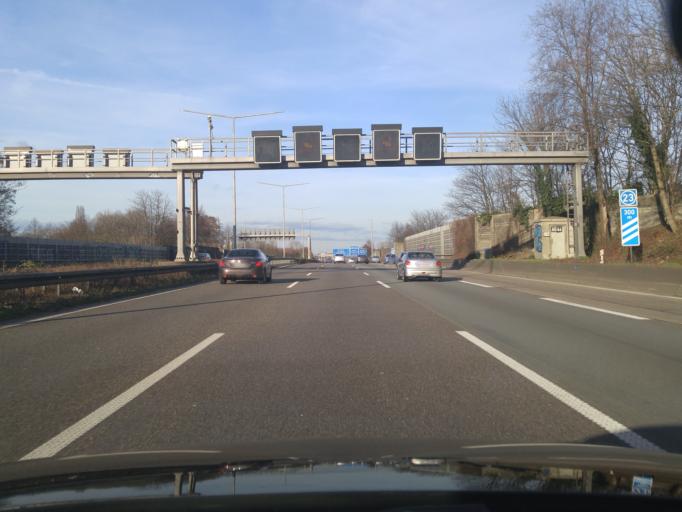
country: DE
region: North Rhine-Westphalia
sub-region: Regierungsbezirk Koln
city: Leverkusen
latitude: 51.0308
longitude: 7.0102
